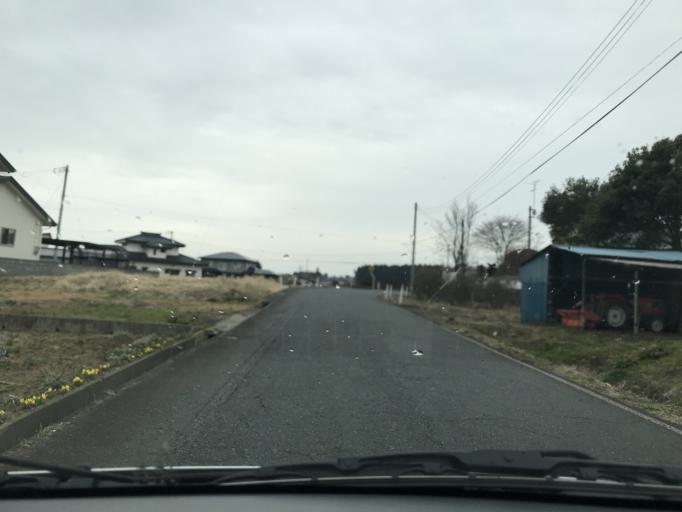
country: JP
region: Iwate
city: Mizusawa
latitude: 39.1275
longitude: 141.1085
